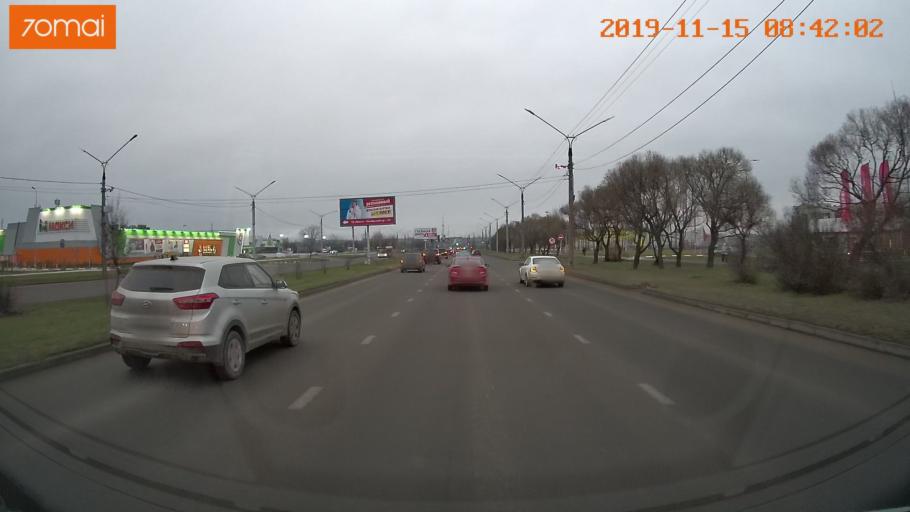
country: RU
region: Vologda
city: Cherepovets
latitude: 59.1000
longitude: 37.9100
